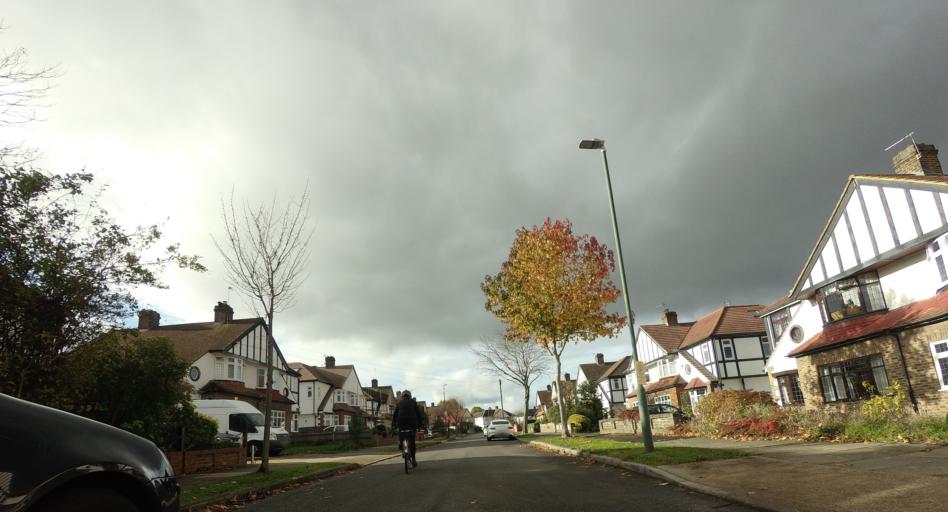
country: GB
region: England
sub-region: Greater London
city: Sidcup
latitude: 51.4331
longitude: 0.1176
